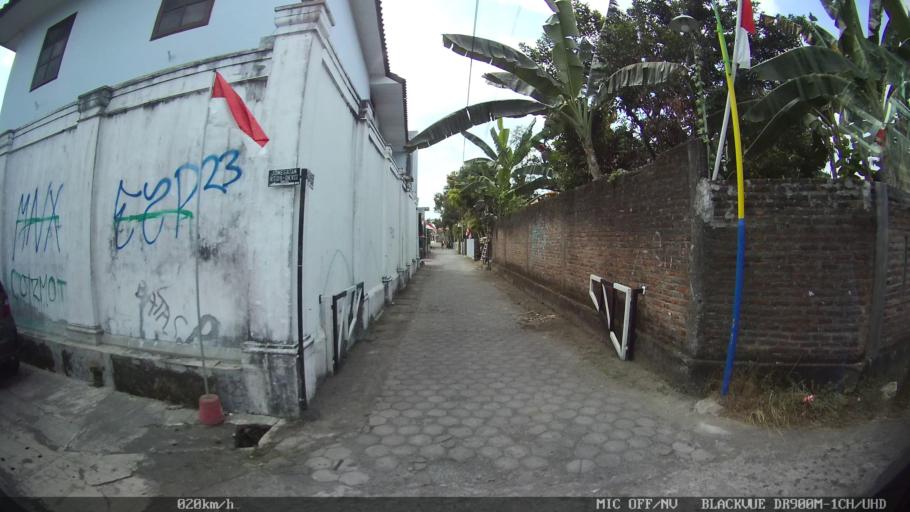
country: ID
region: Daerah Istimewa Yogyakarta
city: Kasihan
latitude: -7.8172
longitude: 110.3479
